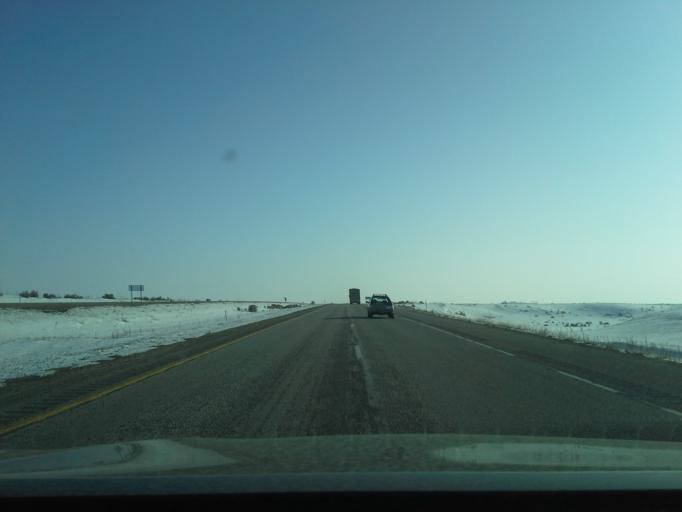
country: US
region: Idaho
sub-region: Oneida County
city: Malad City
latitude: 42.5168
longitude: -112.1705
